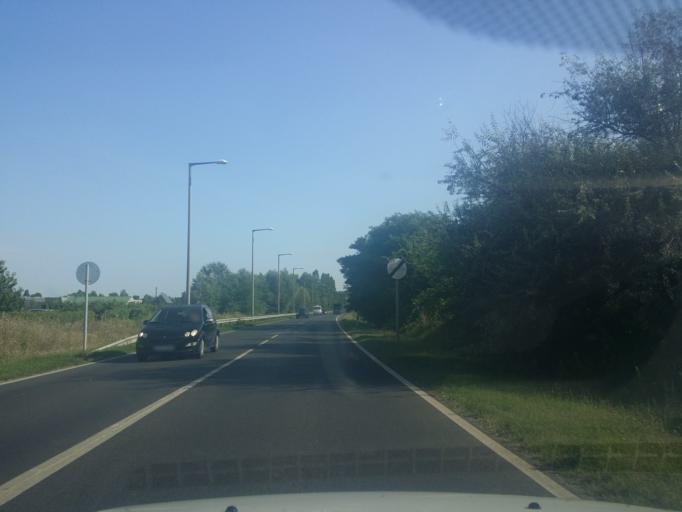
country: HU
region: Bacs-Kiskun
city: Baja
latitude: 46.1906
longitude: 18.9767
